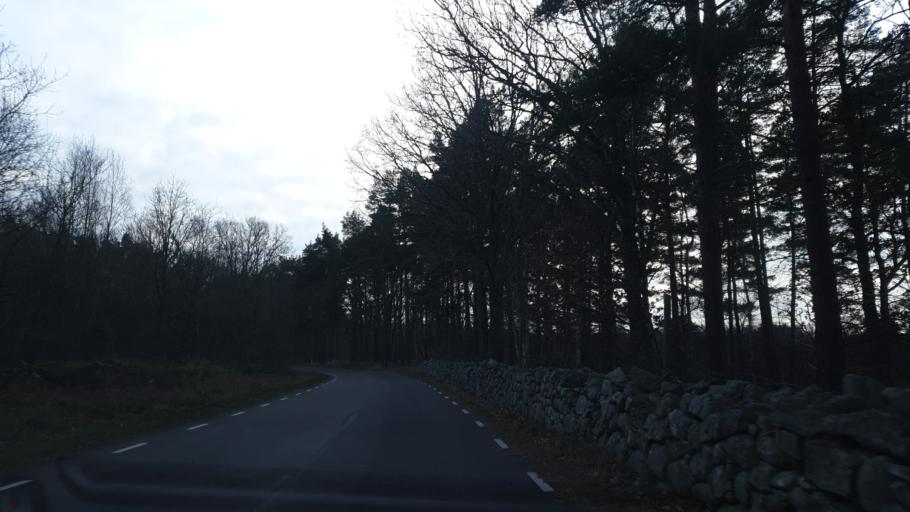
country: SE
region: Blekinge
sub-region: Karlskrona Kommun
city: Jaemjoe
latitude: 56.2208
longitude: 15.9844
